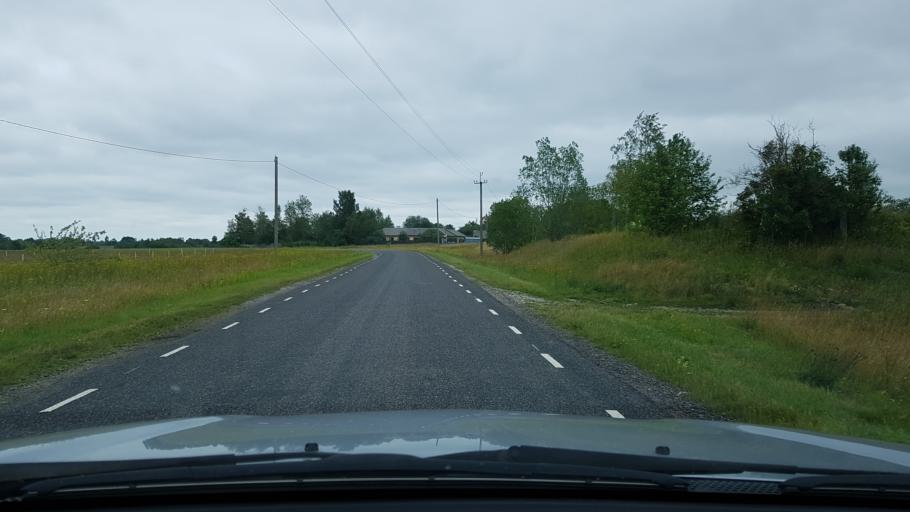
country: EE
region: Ida-Virumaa
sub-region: Narva linn
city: Narva
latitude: 59.3822
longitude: 28.1317
